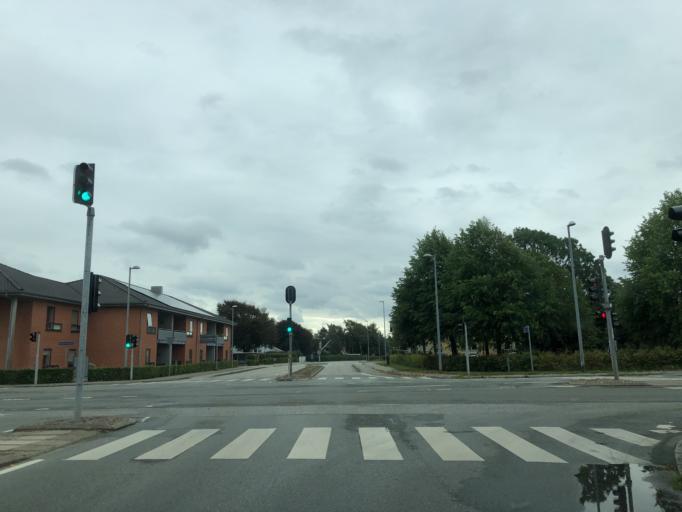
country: DK
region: Central Jutland
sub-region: Herning Kommune
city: Snejbjerg
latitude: 56.1336
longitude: 8.9048
